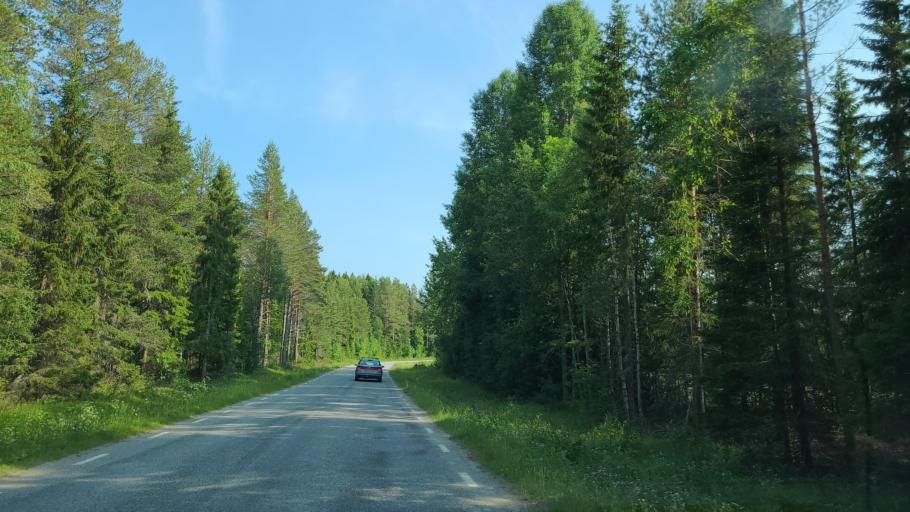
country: SE
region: Vaesterbotten
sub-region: Skelleftea Kommun
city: Burea
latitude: 64.3589
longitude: 21.3364
